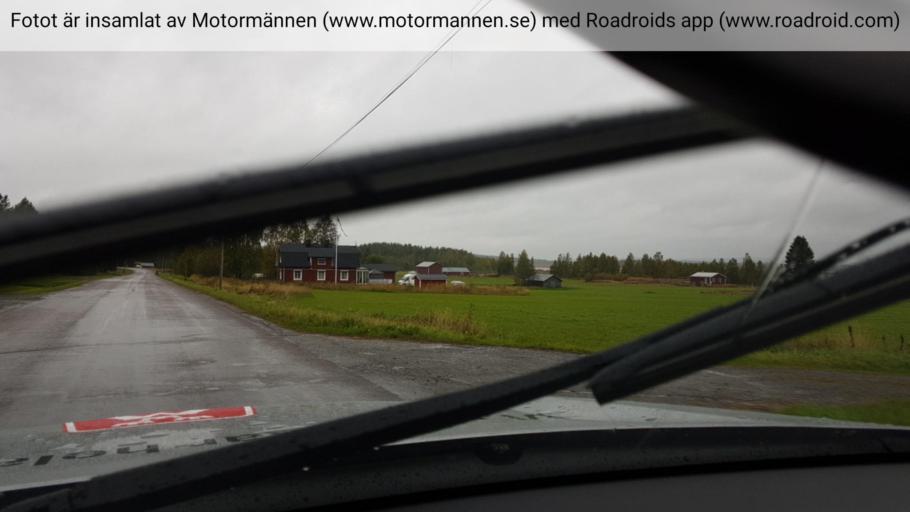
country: SE
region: Norrbotten
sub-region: Lulea Kommun
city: Gammelstad
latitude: 65.7762
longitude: 22.0546
